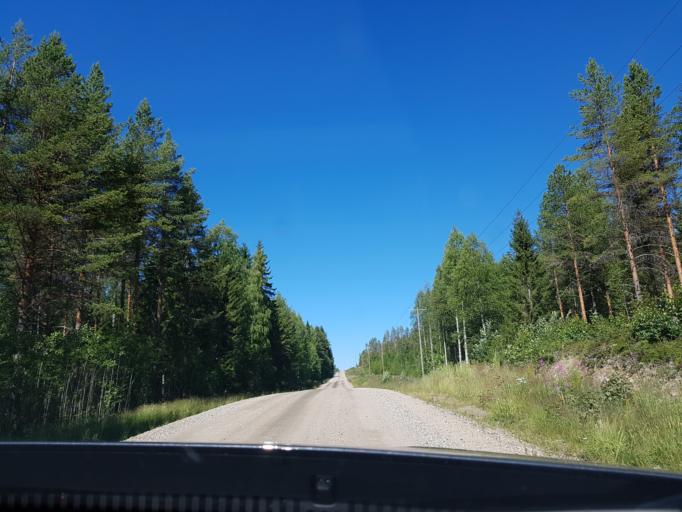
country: FI
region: Kainuu
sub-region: Kehys-Kainuu
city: Kuhmo
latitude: 64.1684
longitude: 29.6491
